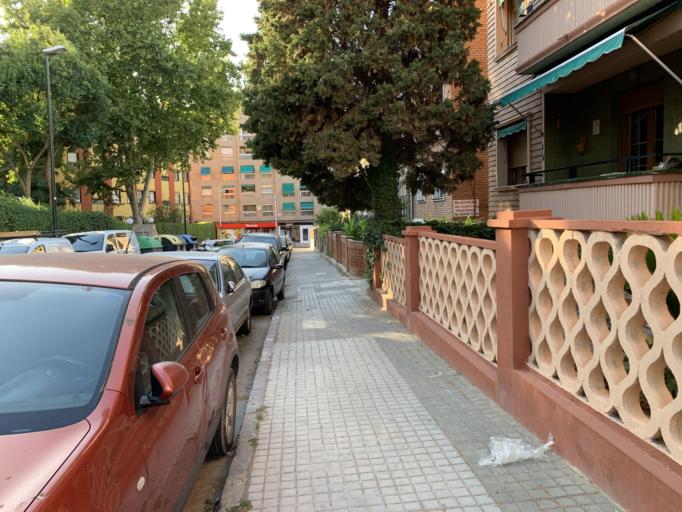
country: ES
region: Aragon
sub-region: Provincia de Zaragoza
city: Delicias
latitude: 41.6375
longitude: -0.8896
